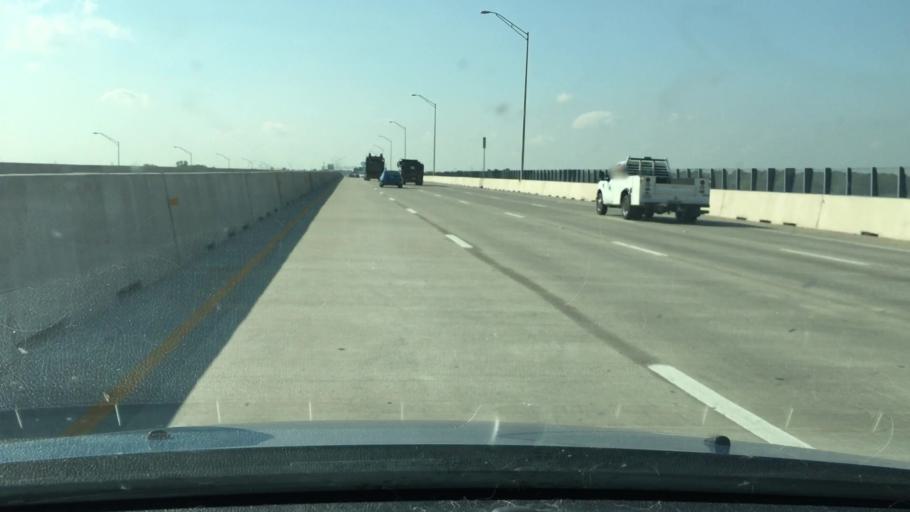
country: US
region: Texas
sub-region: Denton County
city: Lake Dallas
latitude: 33.1035
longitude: -97.0282
